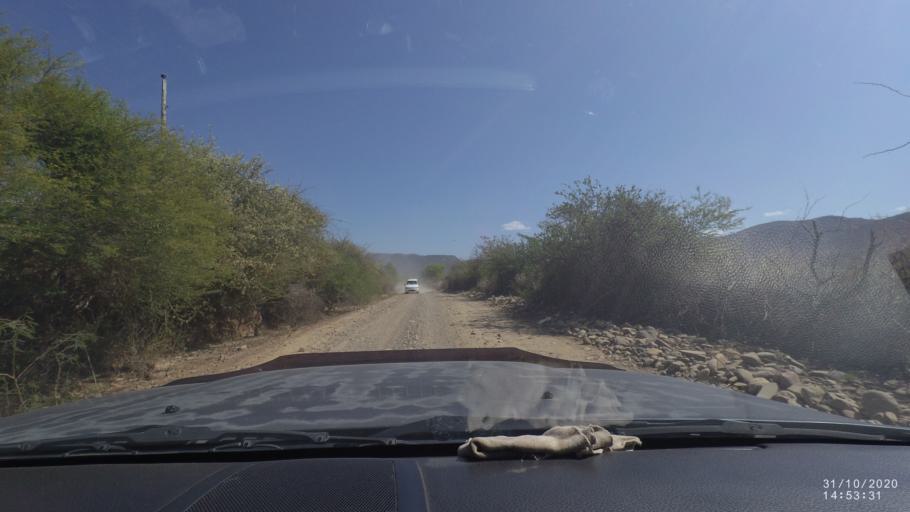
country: BO
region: Cochabamba
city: Aiquile
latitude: -18.2197
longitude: -64.8574
